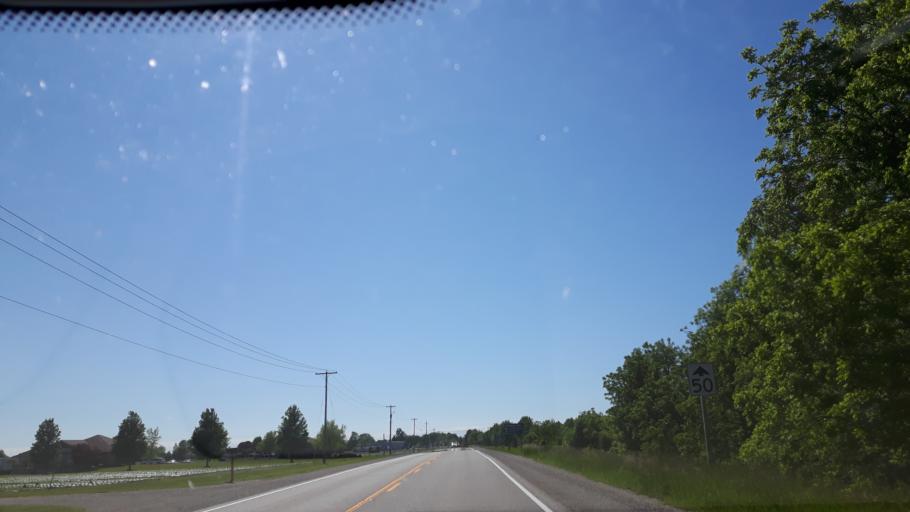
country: CA
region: Ontario
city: Bluewater
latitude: 43.4126
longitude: -81.6967
